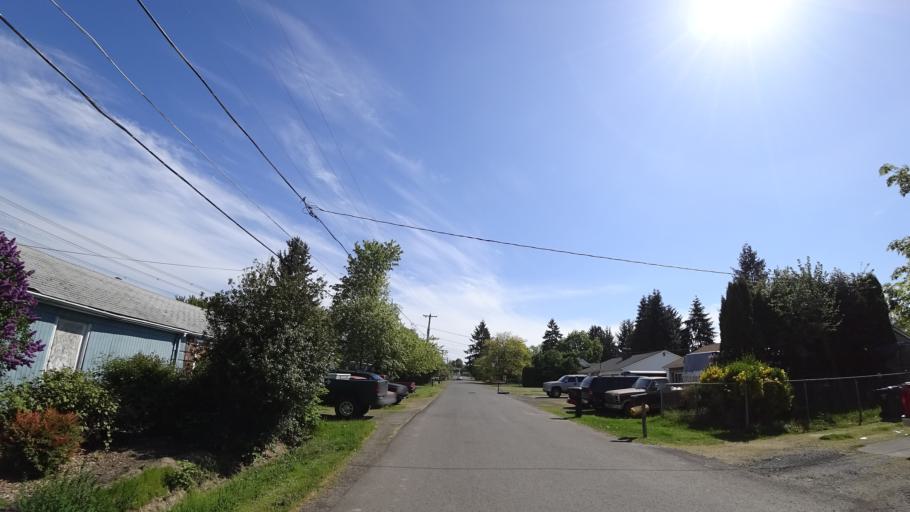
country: US
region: Oregon
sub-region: Washington County
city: Aloha
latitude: 45.5004
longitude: -122.8994
